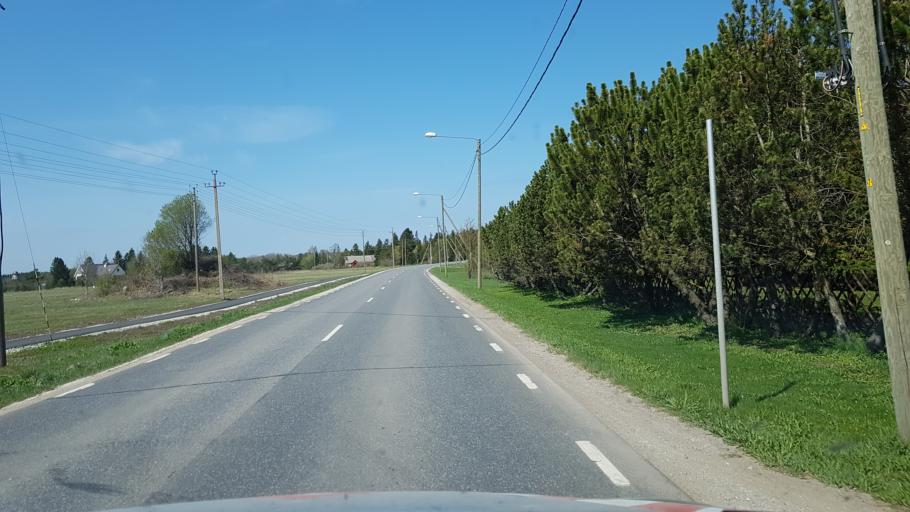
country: EE
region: Harju
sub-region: Harku vald
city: Tabasalu
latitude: 59.4306
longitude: 24.5216
